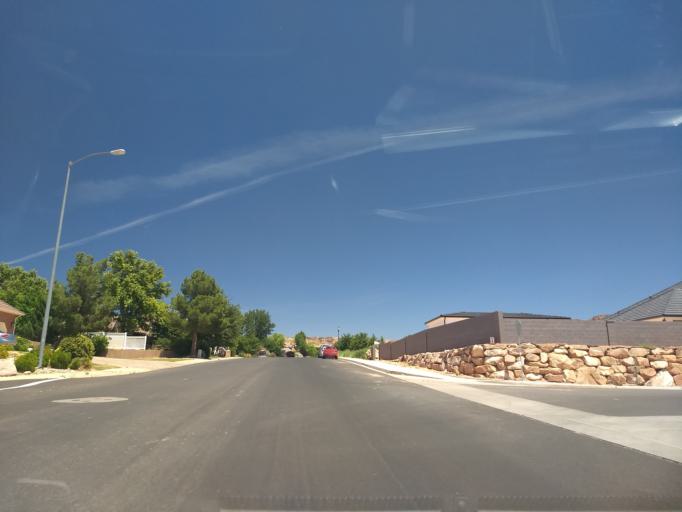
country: US
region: Utah
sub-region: Washington County
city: Washington
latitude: 37.0889
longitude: -113.4926
